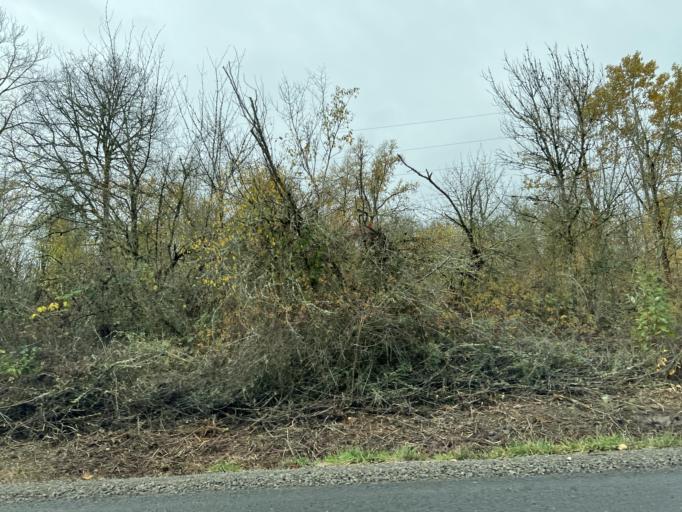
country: US
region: Oregon
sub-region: Polk County
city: Independence
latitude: 44.8039
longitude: -123.0892
